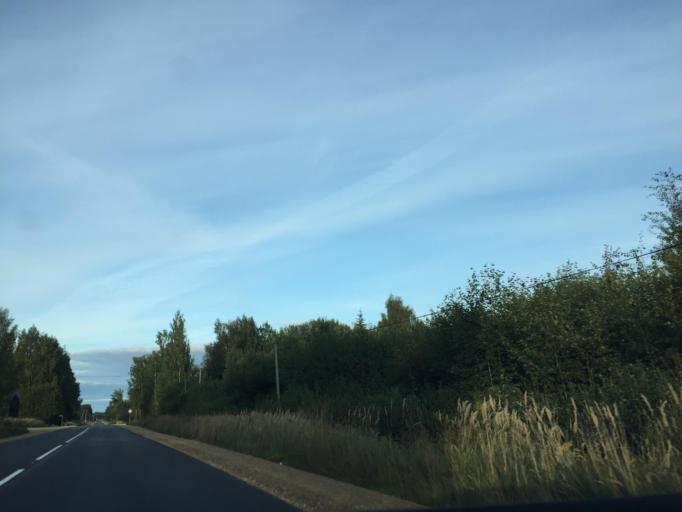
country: LV
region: Viesite
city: Viesite
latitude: 56.3523
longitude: 25.5945
